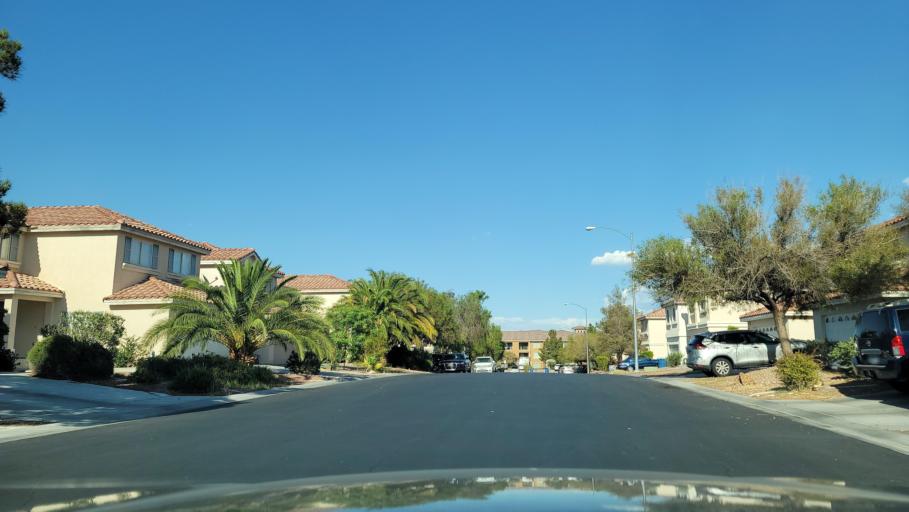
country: US
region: Nevada
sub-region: Clark County
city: Summerlin South
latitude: 36.0931
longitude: -115.3018
